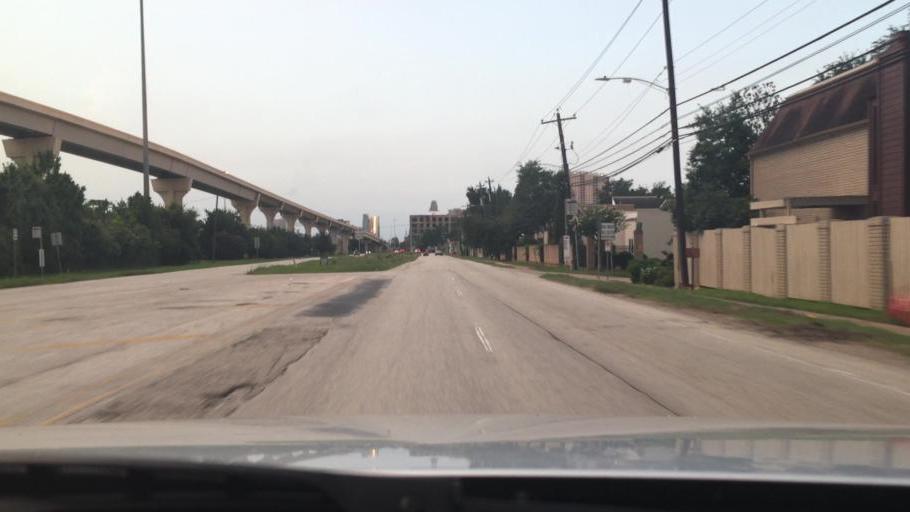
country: US
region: Texas
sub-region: Harris County
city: Hunters Creek Village
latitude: 29.7783
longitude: -95.4568
